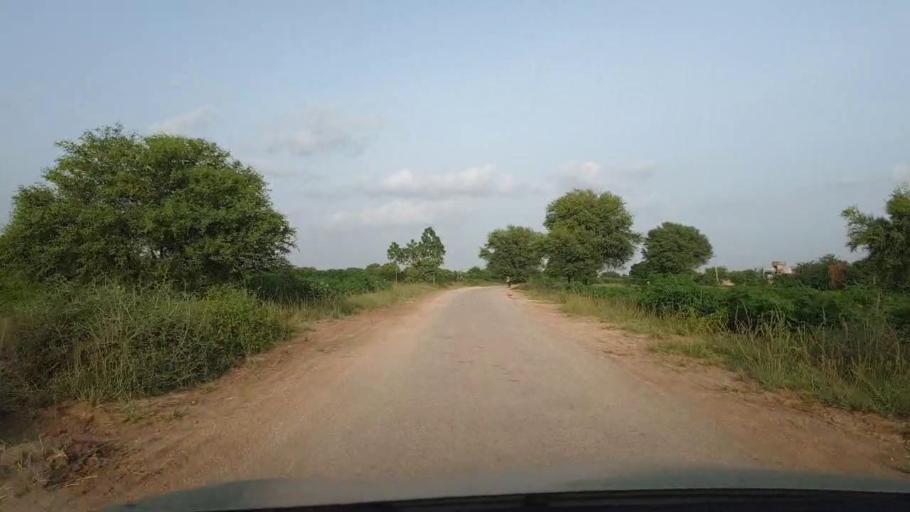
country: PK
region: Sindh
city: Tando Ghulam Ali
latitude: 25.0978
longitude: 68.8869
